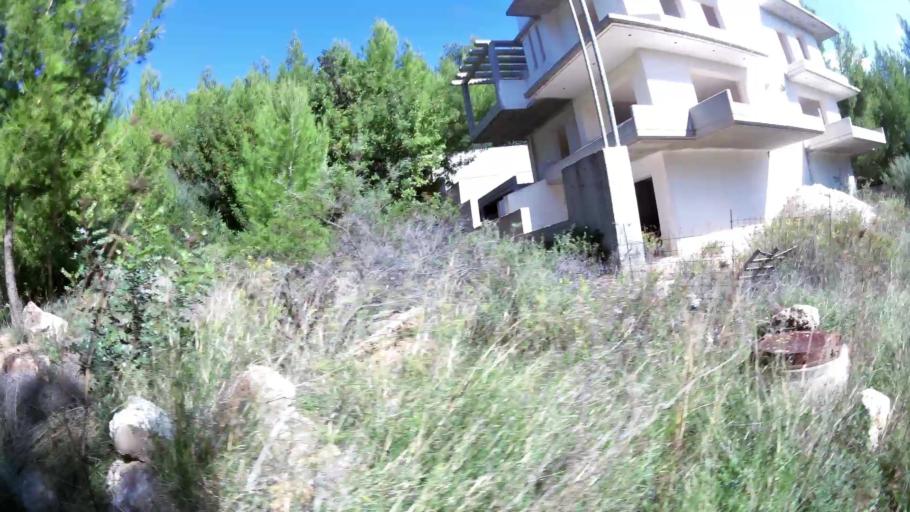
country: GR
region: Attica
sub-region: Nomarchia Anatolikis Attikis
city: Dioni
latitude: 38.0292
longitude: 23.9220
